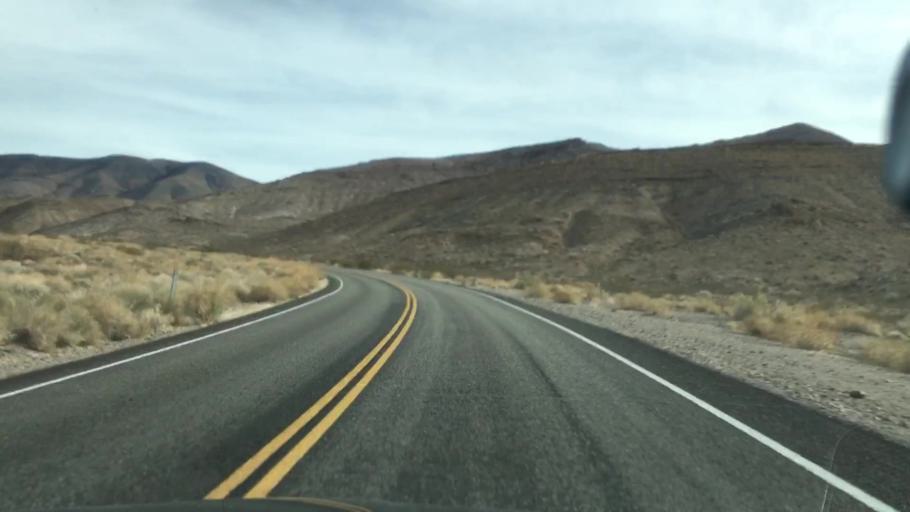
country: US
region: Nevada
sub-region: Nye County
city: Beatty
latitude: 36.7457
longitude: -116.9440
